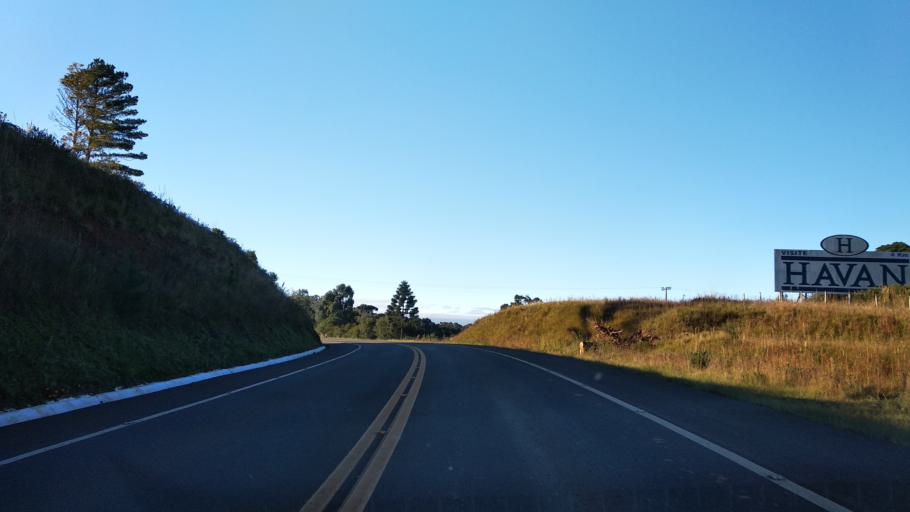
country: BR
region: Santa Catarina
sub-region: Lages
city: Lages
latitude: -27.7924
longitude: -50.4071
